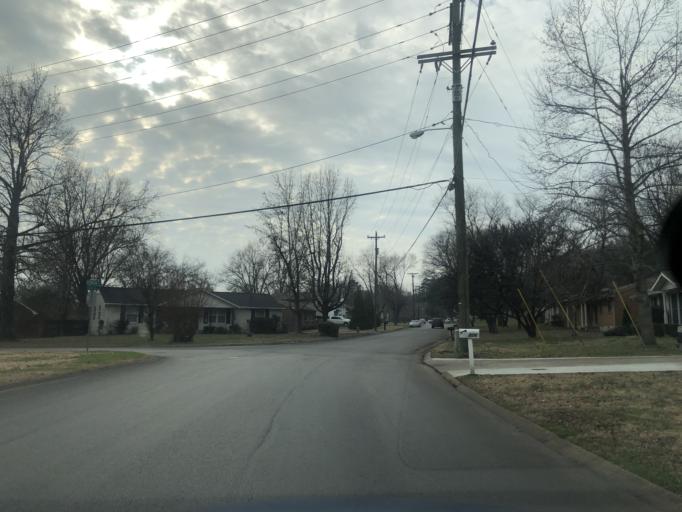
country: US
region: Tennessee
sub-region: Davidson County
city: Oak Hill
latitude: 36.0911
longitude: -86.7212
